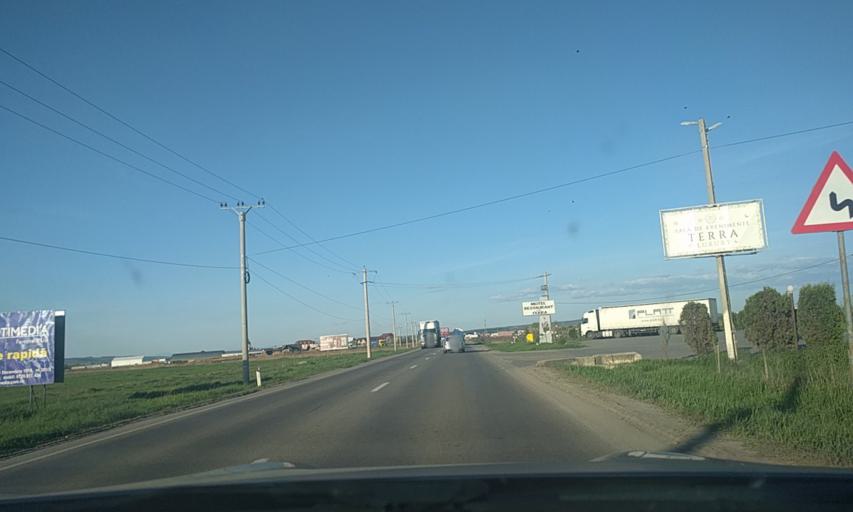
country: RO
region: Mures
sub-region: Comuna Ungheni
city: Ungheni
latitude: 46.4699
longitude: 24.4416
